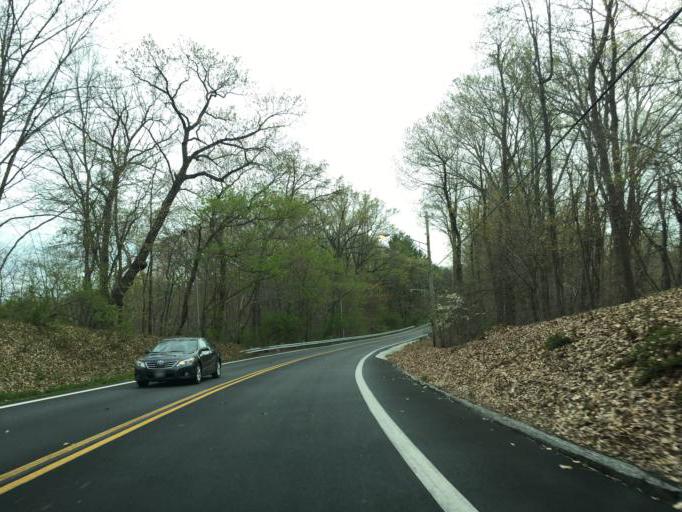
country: US
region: Maryland
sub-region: Baltimore County
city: Hampton
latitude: 39.4740
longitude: -76.5744
